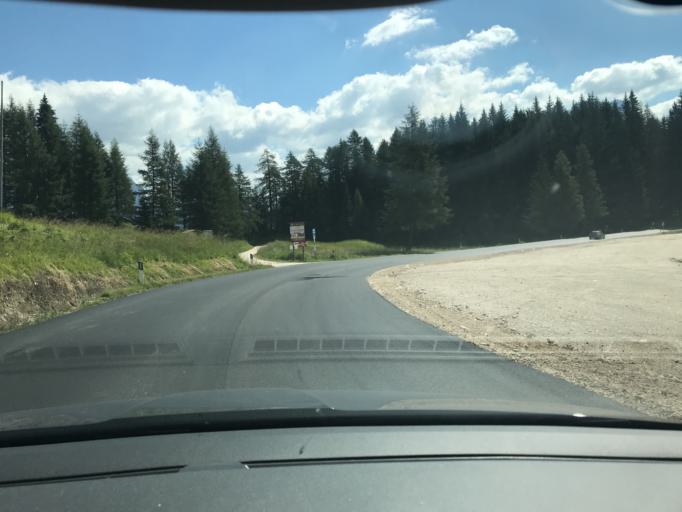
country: IT
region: Veneto
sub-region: Provincia di Belluno
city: Cortina d'Ampezzo
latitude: 46.5225
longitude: 12.0982
